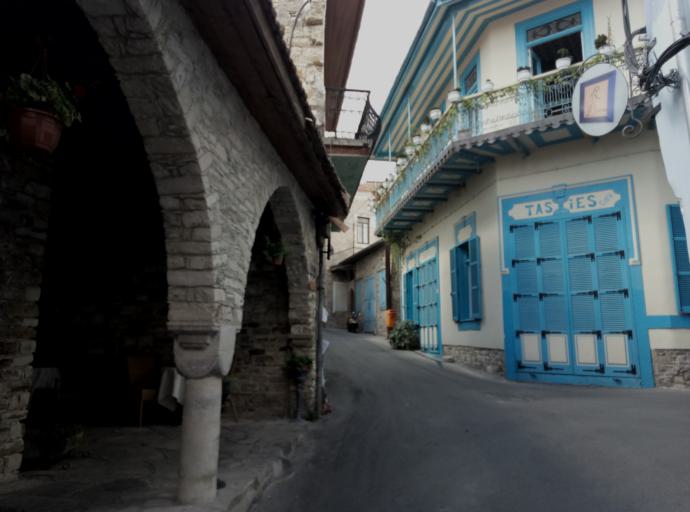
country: CY
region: Lefkosia
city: Lythrodontas
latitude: 34.8658
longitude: 33.3074
